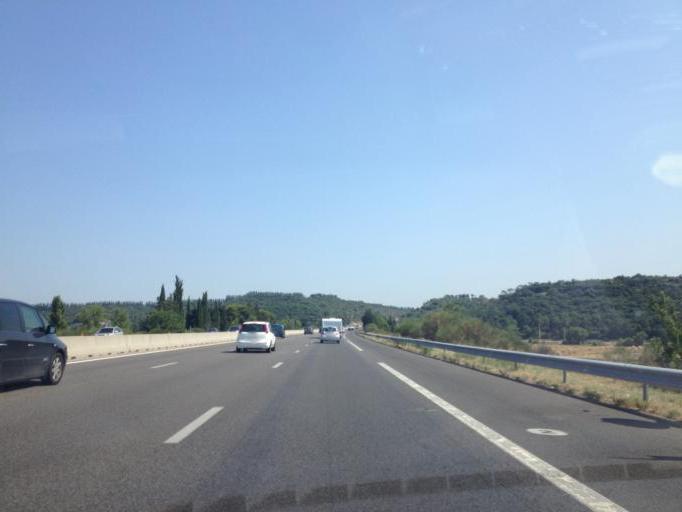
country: FR
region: Rhone-Alpes
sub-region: Departement de la Drome
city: Donzere
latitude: 44.4185
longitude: 4.7330
